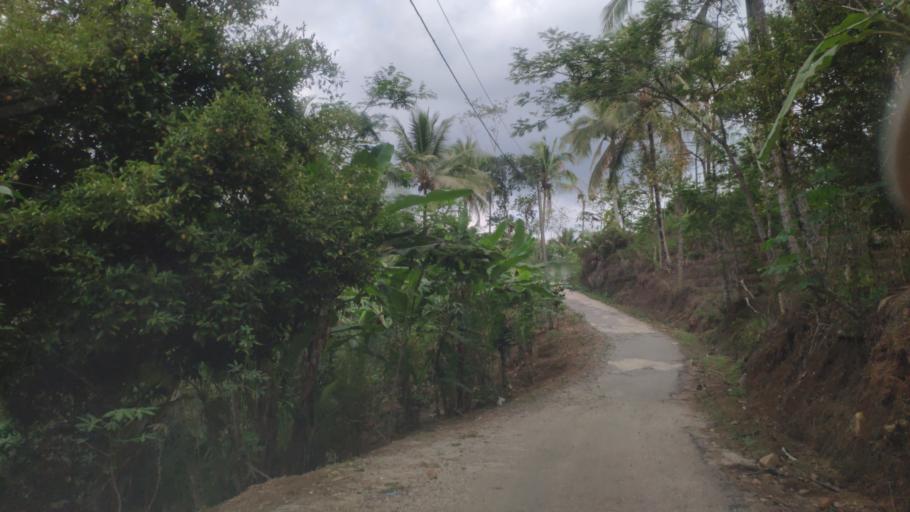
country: ID
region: Central Java
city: Purbalingga
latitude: -7.3058
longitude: 109.5813
